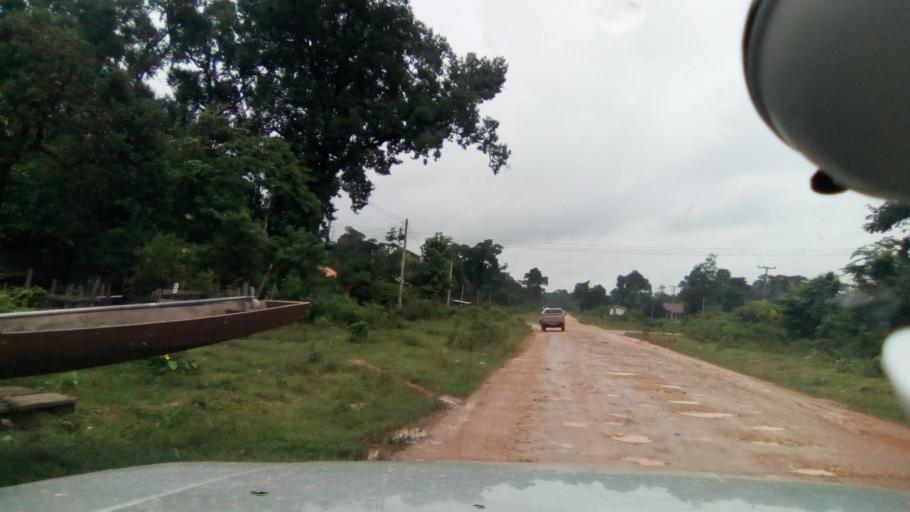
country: LA
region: Attapu
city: Attapu
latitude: 14.6747
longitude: 106.5747
